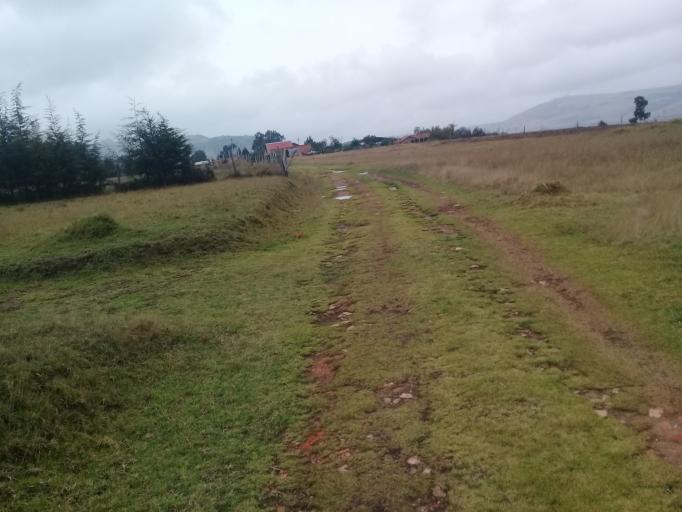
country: CO
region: Boyaca
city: Siachoque
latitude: 5.5619
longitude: -73.2788
